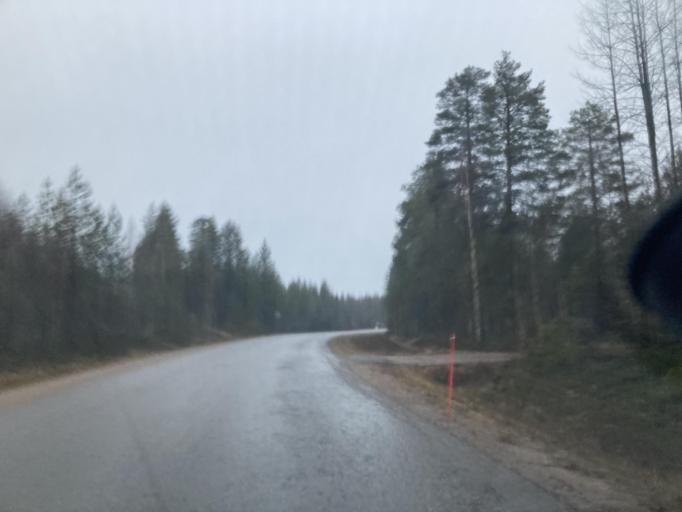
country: FI
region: Lapland
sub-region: Rovaniemi
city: Rovaniemi
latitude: 66.5930
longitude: 25.7920
